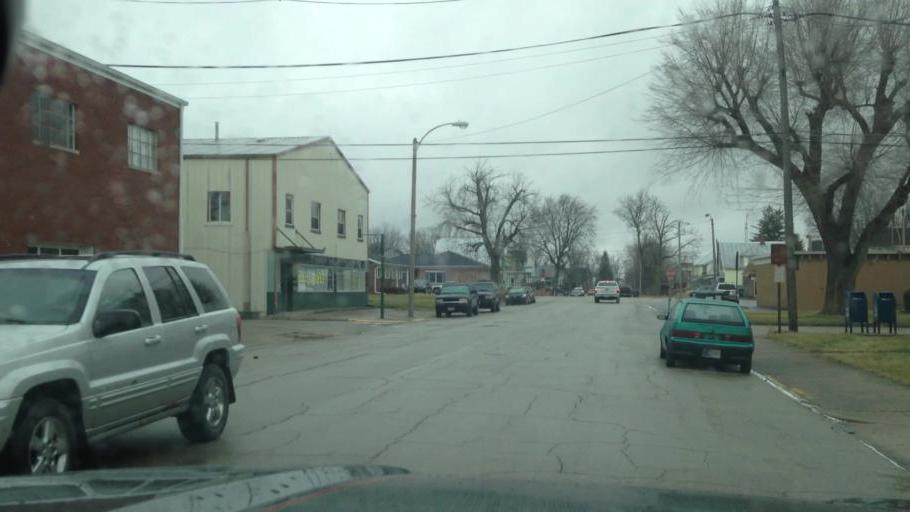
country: US
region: Ohio
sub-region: Darke County
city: Union City
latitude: 40.1994
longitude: -84.8065
